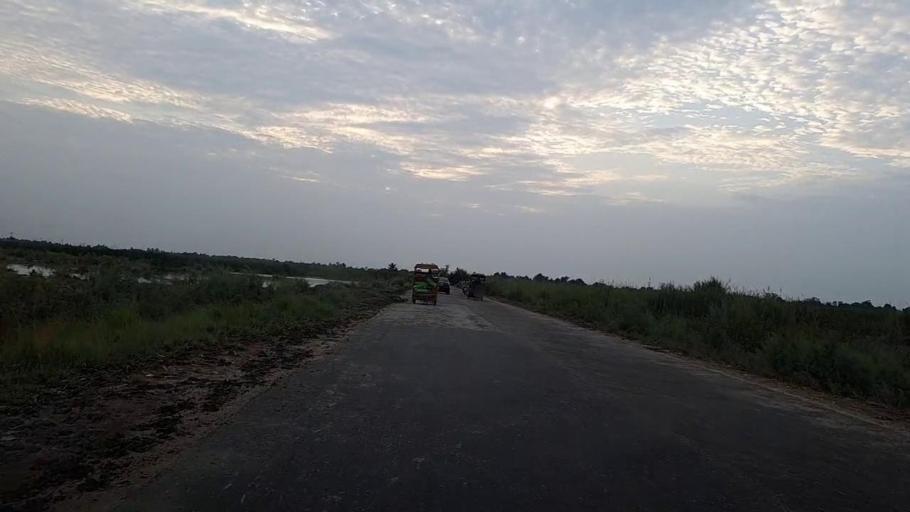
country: PK
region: Sindh
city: Naushahro Firoz
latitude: 26.8146
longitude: 68.1855
